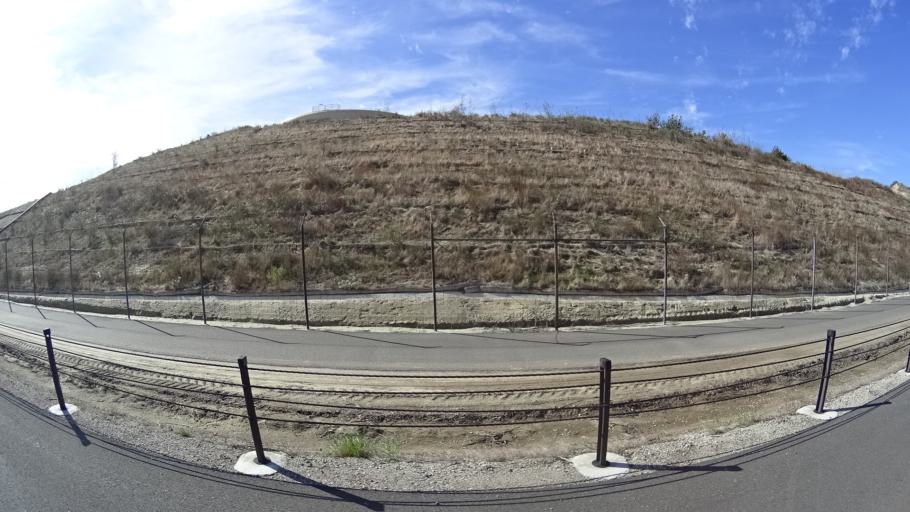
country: US
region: California
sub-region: Orange County
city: Ladera Ranch
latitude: 33.5581
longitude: -117.6017
